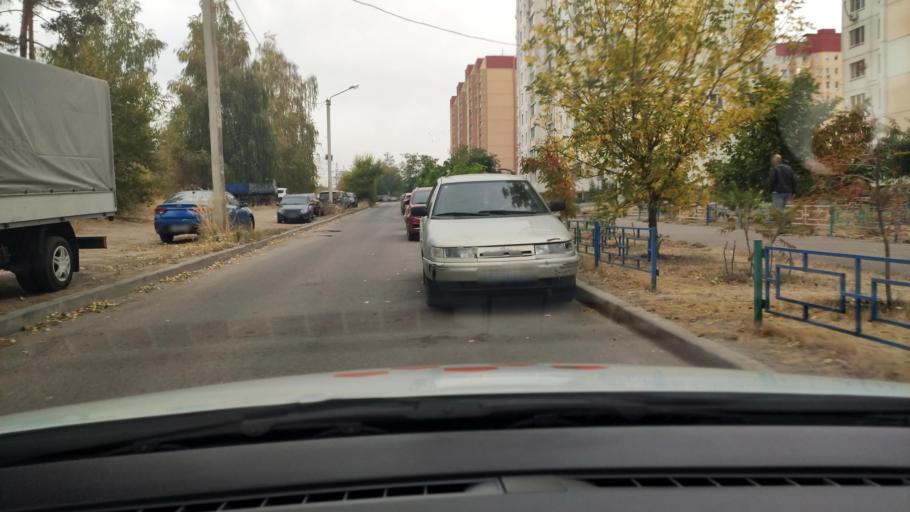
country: RU
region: Voronezj
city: Pridonskoy
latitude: 51.6784
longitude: 39.1213
